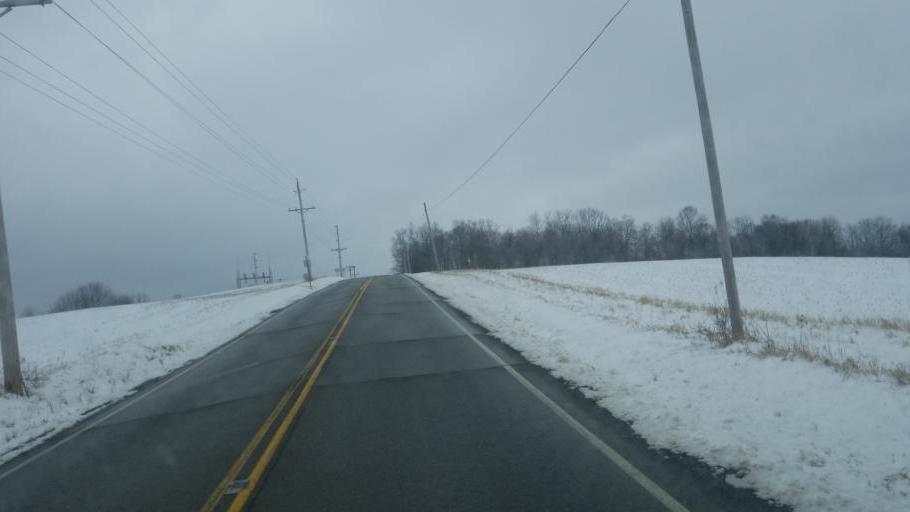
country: US
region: Ohio
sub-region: Knox County
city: Oak Hill
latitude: 40.4637
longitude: -82.1297
